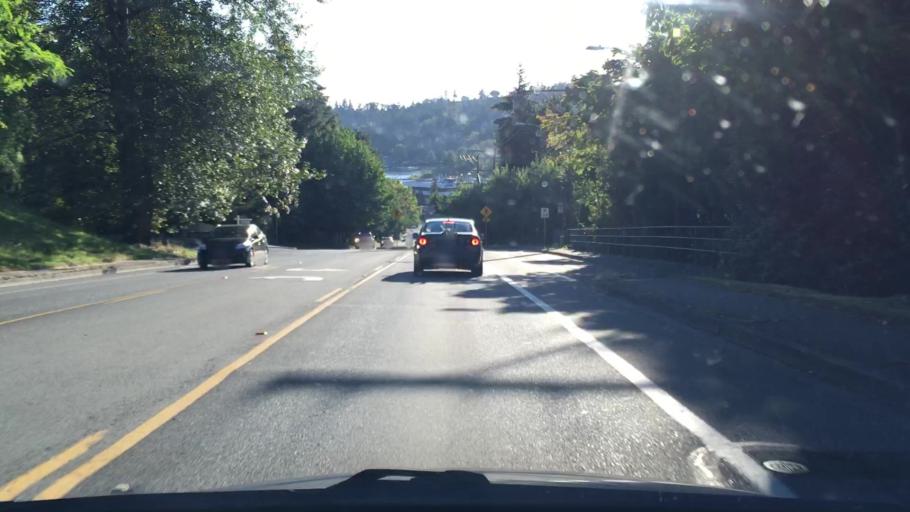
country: US
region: Washington
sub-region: King County
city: Kirkland
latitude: 47.7040
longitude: -122.2053
